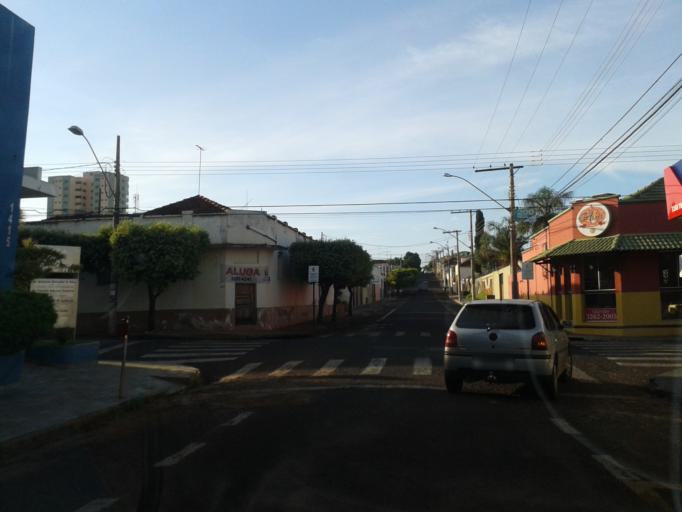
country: BR
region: Minas Gerais
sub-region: Ituiutaba
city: Ituiutaba
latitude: -18.9764
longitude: -49.4632
